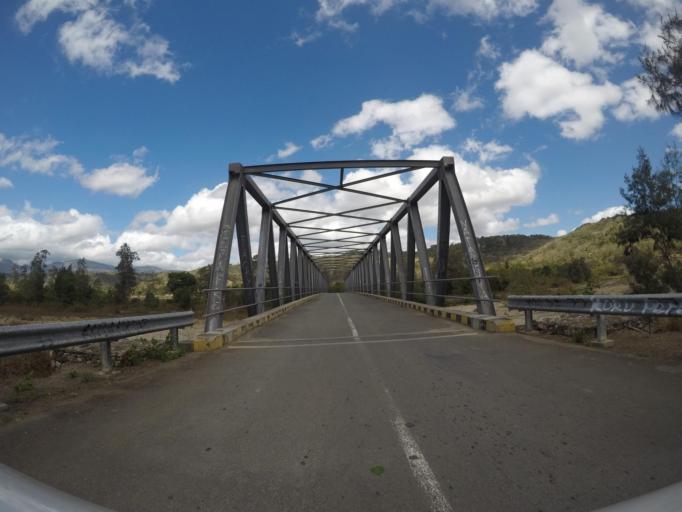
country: TL
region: Lautem
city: Lospalos
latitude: -8.4668
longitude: 126.8204
